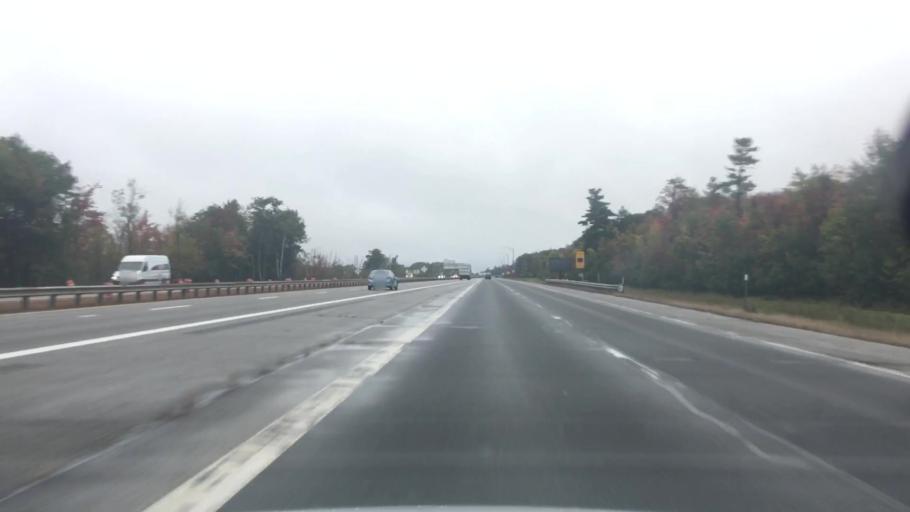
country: US
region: Maine
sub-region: Kennebec County
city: Gardiner
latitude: 44.2209
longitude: -69.8207
